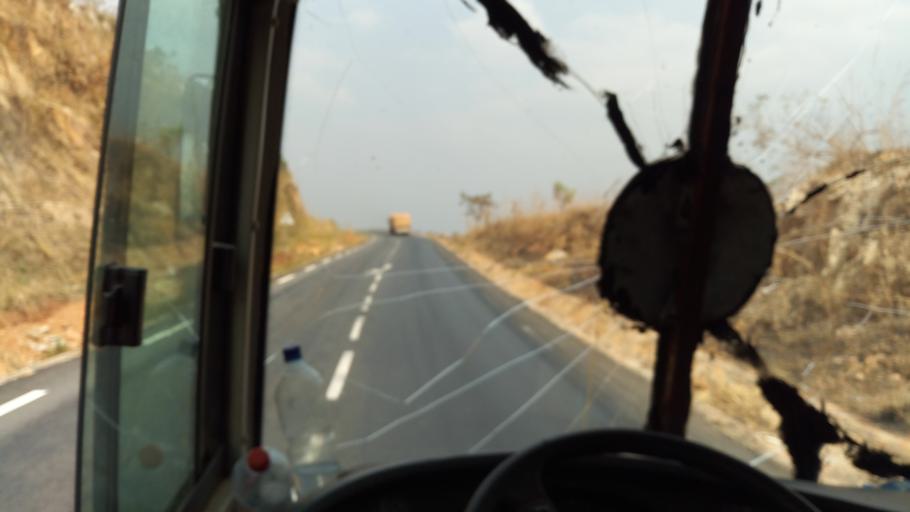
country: TG
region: Kara
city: Bafilo
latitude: 9.2561
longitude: 1.2234
